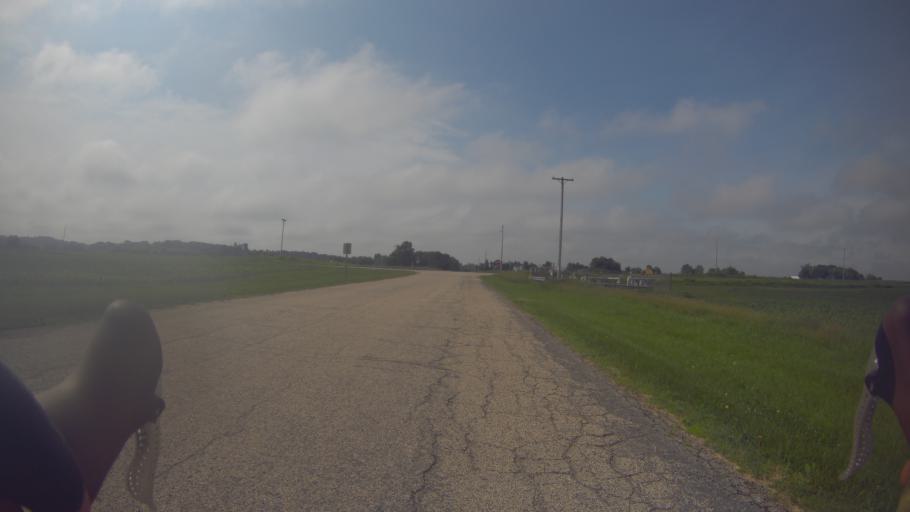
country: US
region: Wisconsin
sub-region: Dane County
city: Stoughton
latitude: 42.9418
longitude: -89.1814
